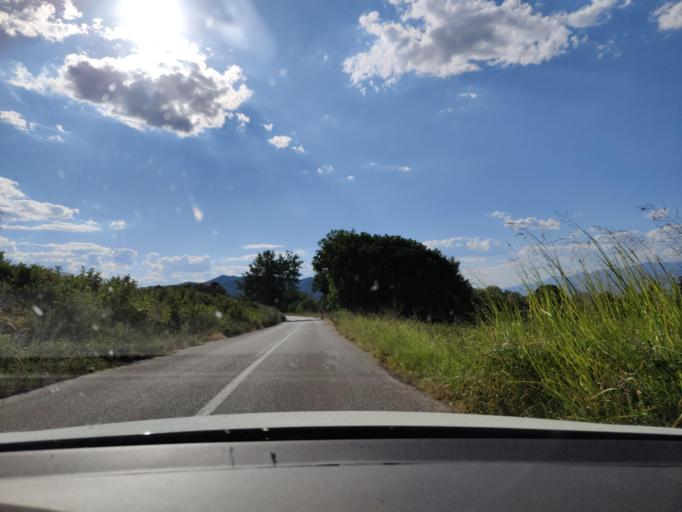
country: GR
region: Central Macedonia
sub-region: Nomos Serron
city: Chrysochorafa
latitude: 41.1783
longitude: 23.1271
